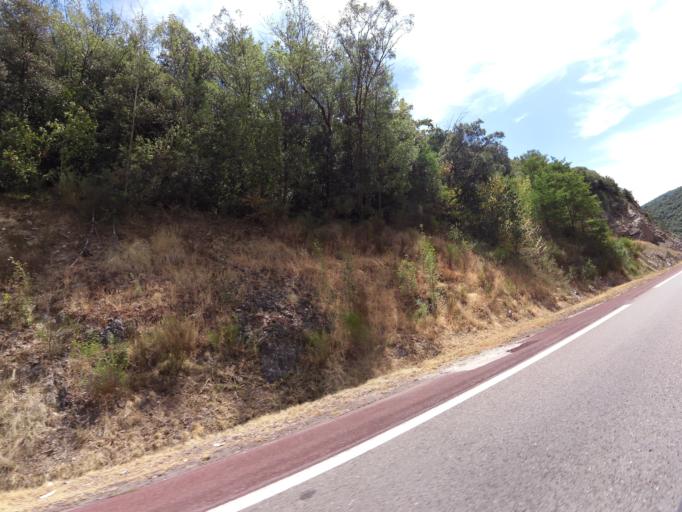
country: FR
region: Languedoc-Roussillon
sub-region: Departement du Gard
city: Sumene
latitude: 43.9859
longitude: 3.6862
